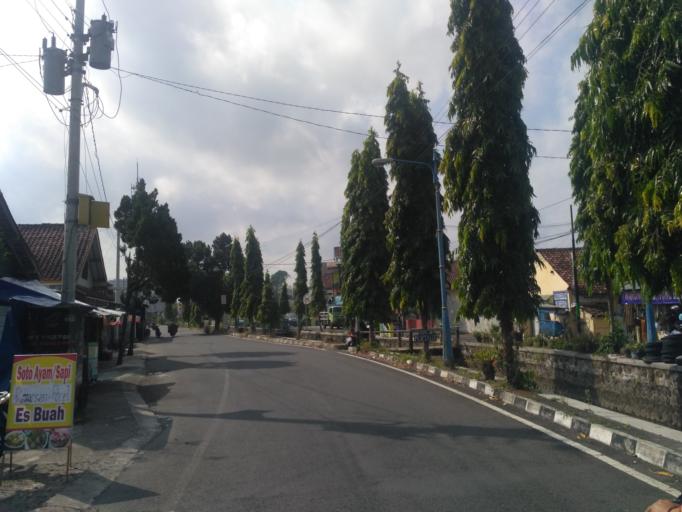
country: ID
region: Daerah Istimewa Yogyakarta
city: Yogyakarta
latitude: -7.7618
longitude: 110.3649
